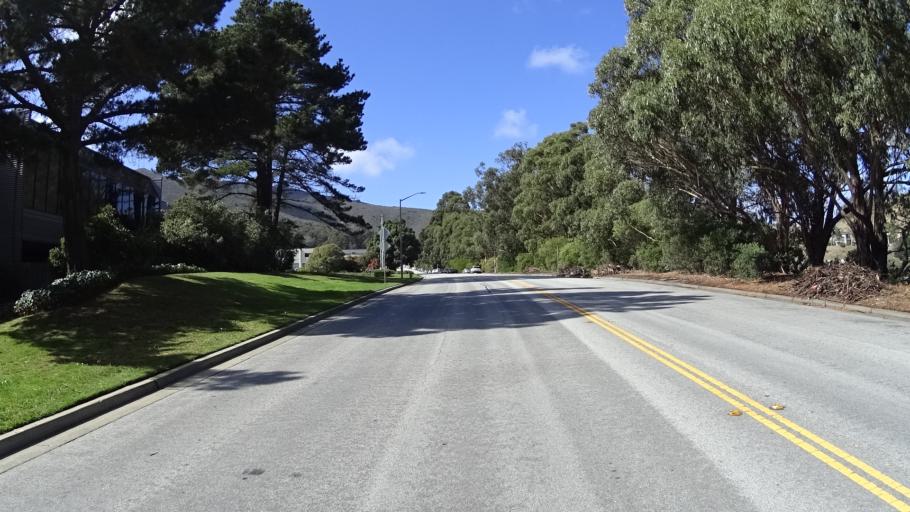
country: US
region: California
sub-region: San Mateo County
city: Brisbane
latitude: 37.6884
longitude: -122.4153
